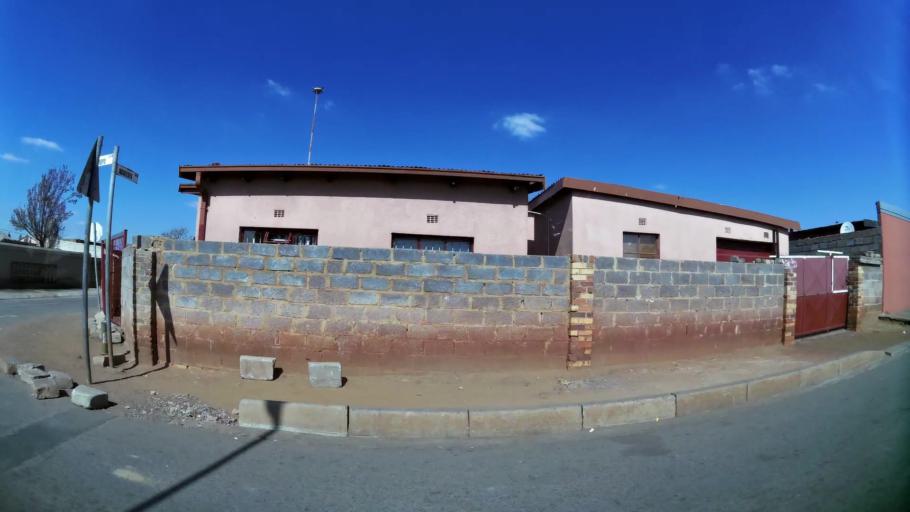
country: ZA
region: Gauteng
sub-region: City of Johannesburg Metropolitan Municipality
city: Soweto
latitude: -26.2530
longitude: 27.8862
